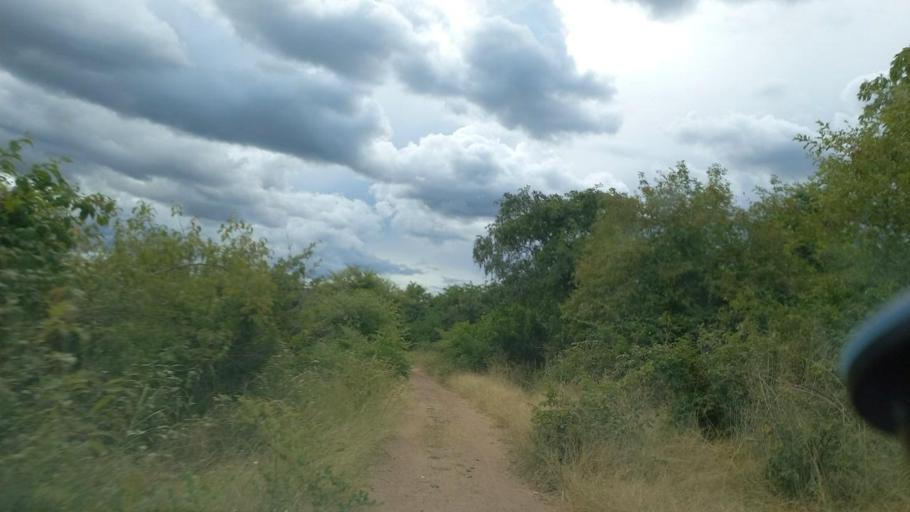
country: ZM
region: Lusaka
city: Luangwa
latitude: -15.6483
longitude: 30.3380
